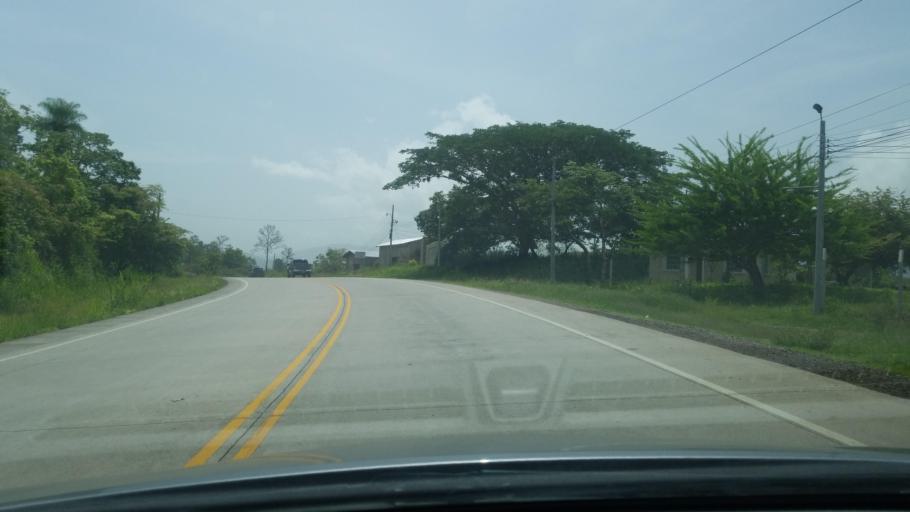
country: HN
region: Copan
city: La Entrada
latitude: 15.0683
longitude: -88.7786
